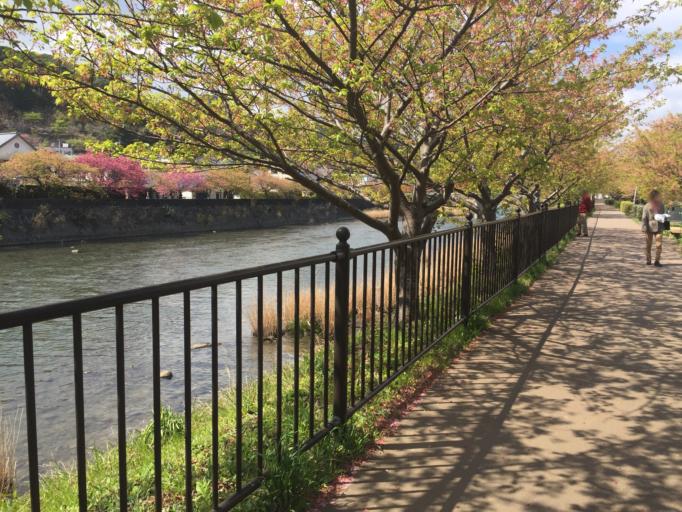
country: JP
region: Shizuoka
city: Shimoda
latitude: 34.7446
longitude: 138.9958
